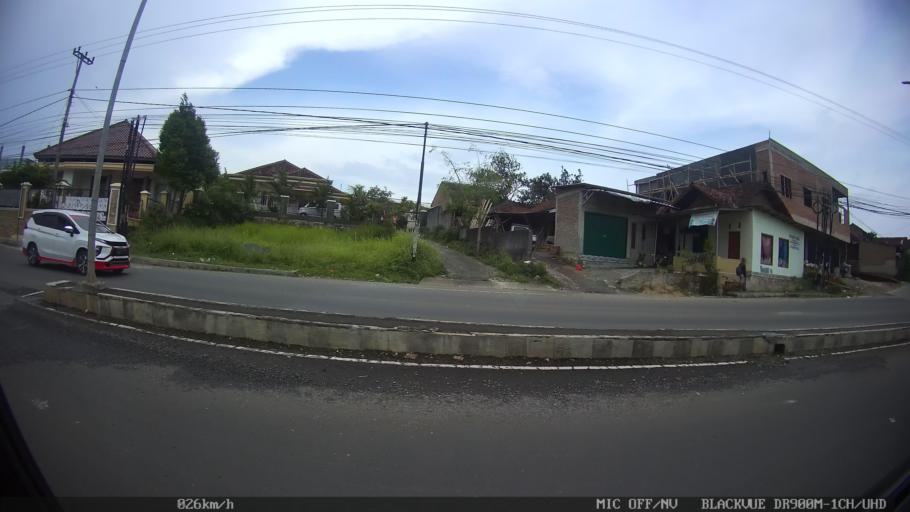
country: ID
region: Lampung
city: Kedaton
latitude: -5.3906
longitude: 105.2191
